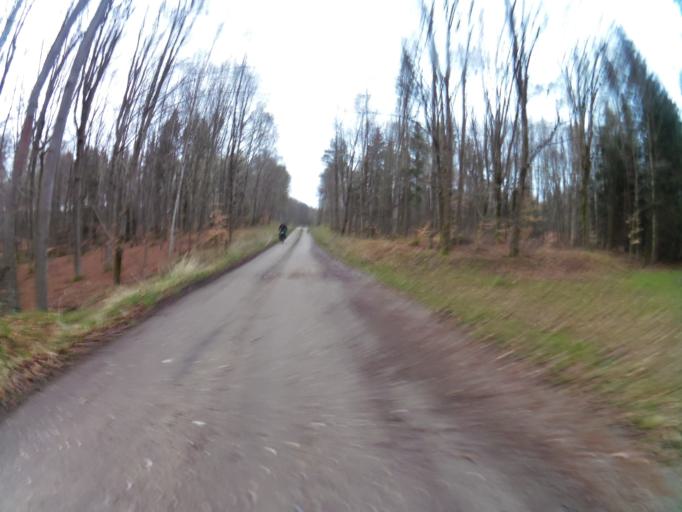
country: PL
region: West Pomeranian Voivodeship
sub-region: Powiat szczecinecki
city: Borne Sulinowo
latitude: 53.6572
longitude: 16.5215
